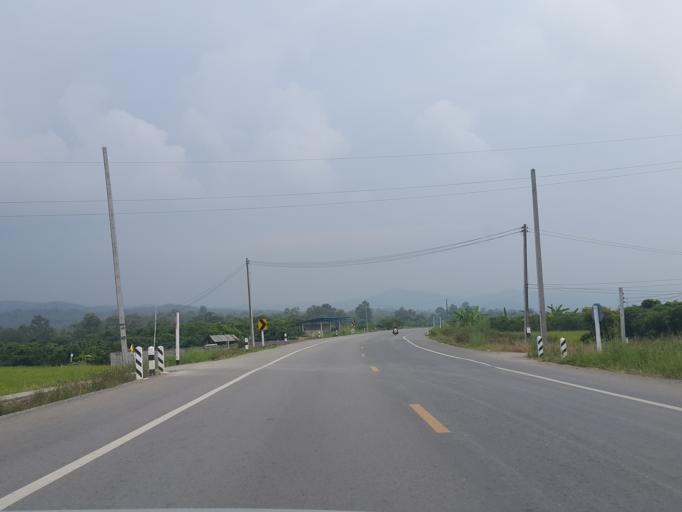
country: TH
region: Chiang Mai
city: Mae Taeng
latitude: 19.0701
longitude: 98.9546
